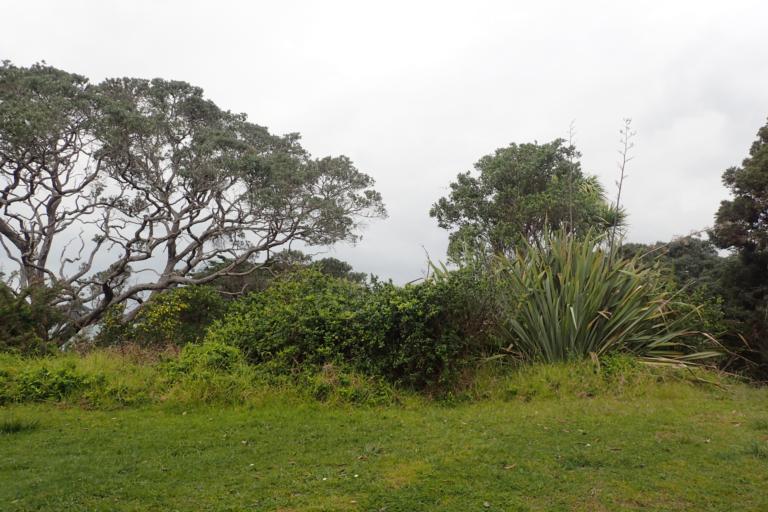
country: NZ
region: Auckland
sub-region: Auckland
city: Pakuranga
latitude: -36.7912
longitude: 175.0073
